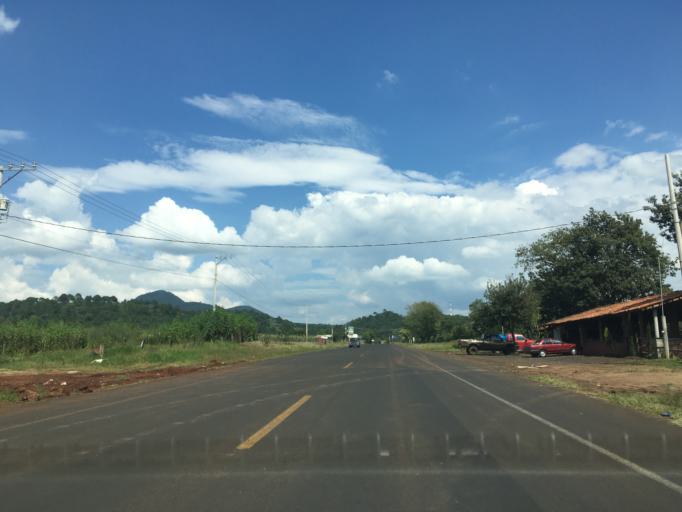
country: MX
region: Michoacan
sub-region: Tingueindin
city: Tingueindin
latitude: 19.8420
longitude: -102.4833
